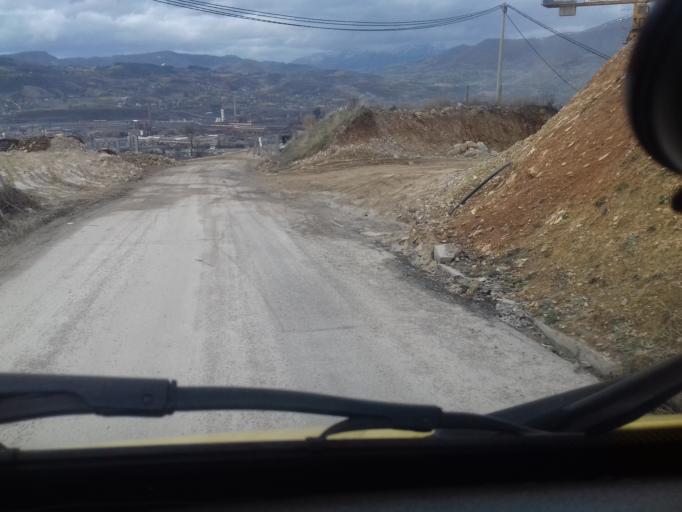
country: BA
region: Federation of Bosnia and Herzegovina
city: Zenica
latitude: 44.2138
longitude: 17.9326
